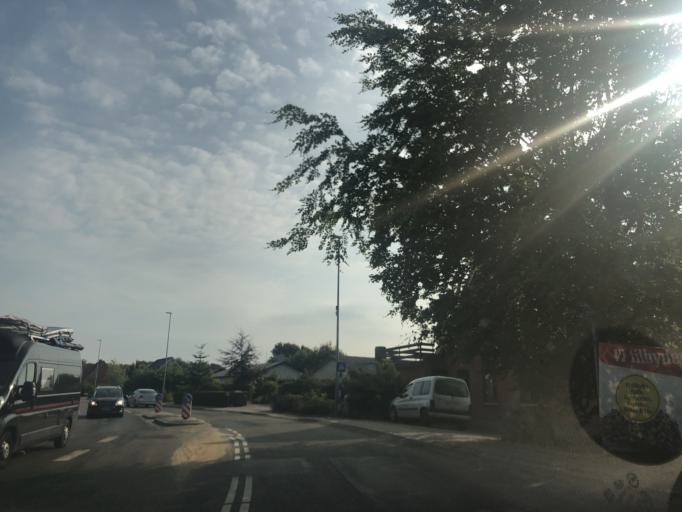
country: DK
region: Central Jutland
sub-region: Skive Kommune
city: Skive
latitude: 56.6538
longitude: 8.9333
